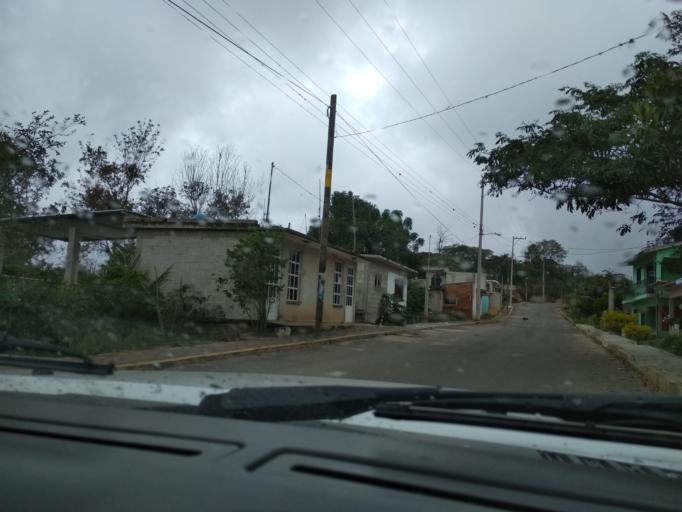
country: MX
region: Veracruz
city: El Castillo
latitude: 19.5401
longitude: -96.8241
